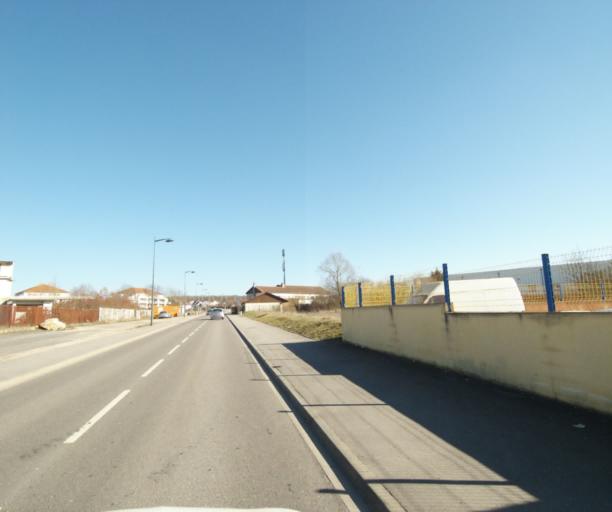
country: FR
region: Lorraine
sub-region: Departement de Meurthe-et-Moselle
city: Tomblaine
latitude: 48.6760
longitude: 6.2246
